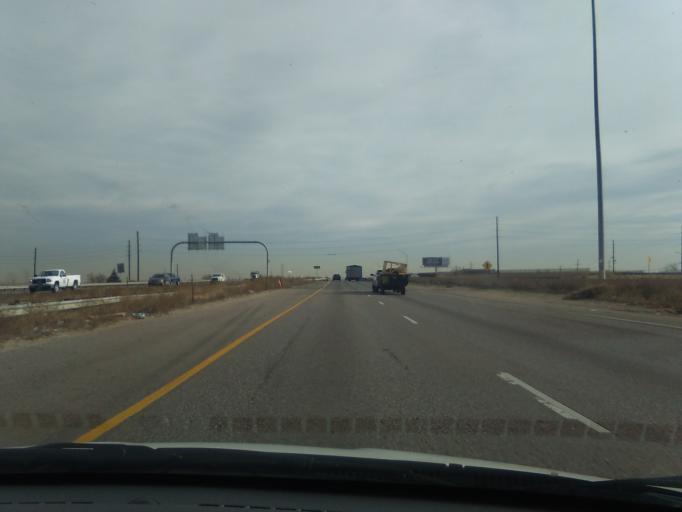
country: US
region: Colorado
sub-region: Adams County
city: Welby
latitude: 39.8241
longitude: -104.9614
